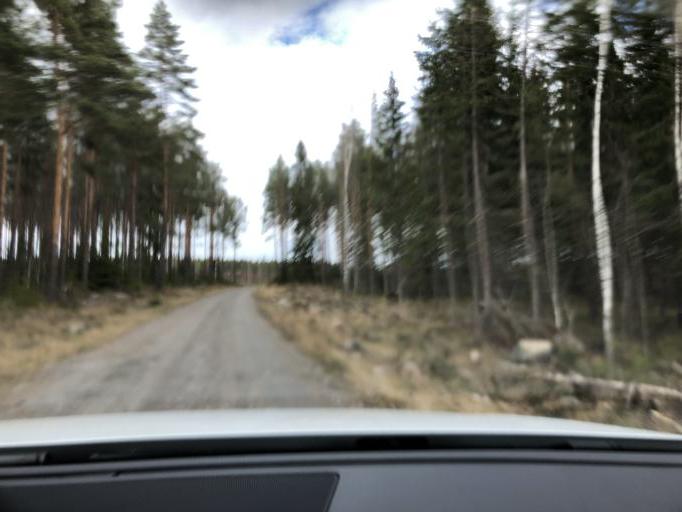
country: SE
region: Gaevleborg
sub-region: Gavle Kommun
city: Hedesunda
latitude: 60.3221
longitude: 17.1030
